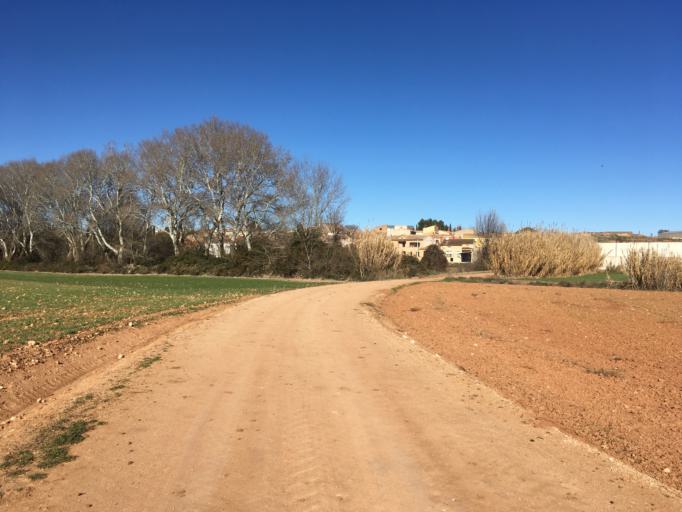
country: ES
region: Castille-La Mancha
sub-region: Provincia de Cuenca
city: Atalaya del Canavate
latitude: 39.5459
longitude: -2.2471
